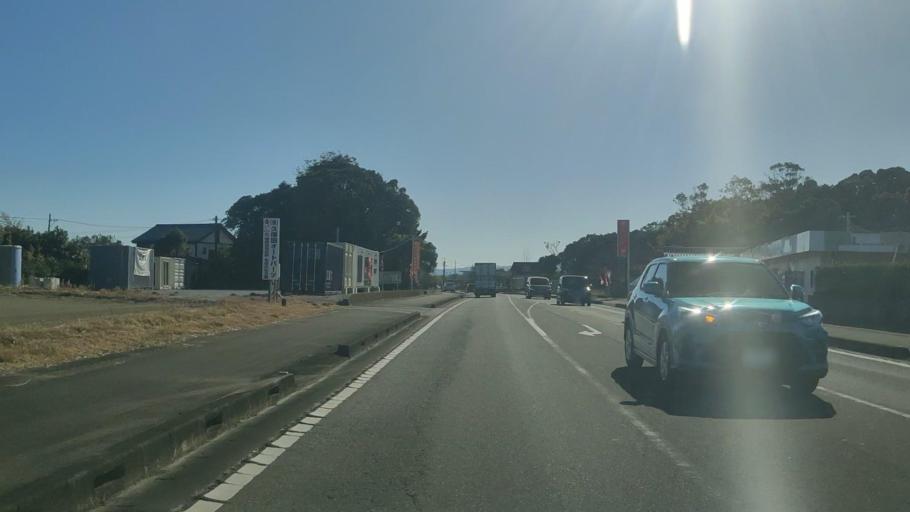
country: JP
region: Miyazaki
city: Miyazaki-shi
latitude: 31.9510
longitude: 131.4603
